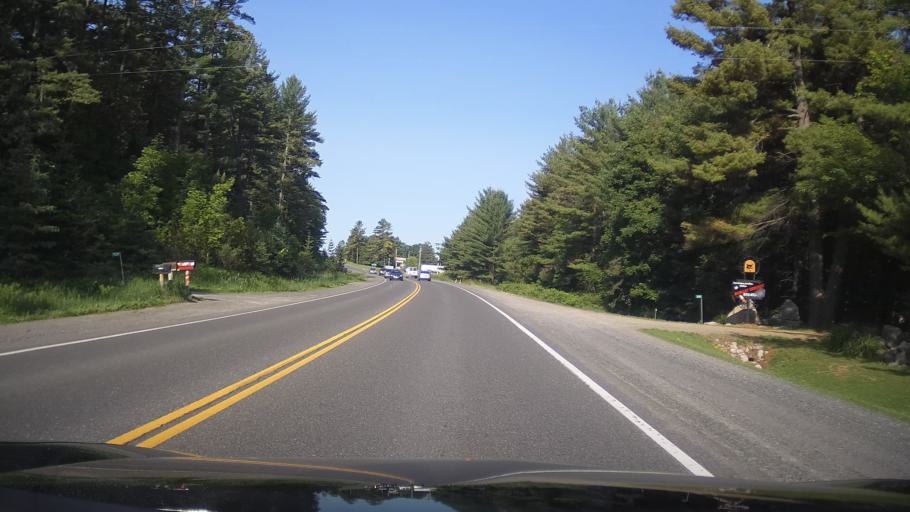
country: CA
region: Ontario
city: Quinte West
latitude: 44.4582
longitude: -77.7605
